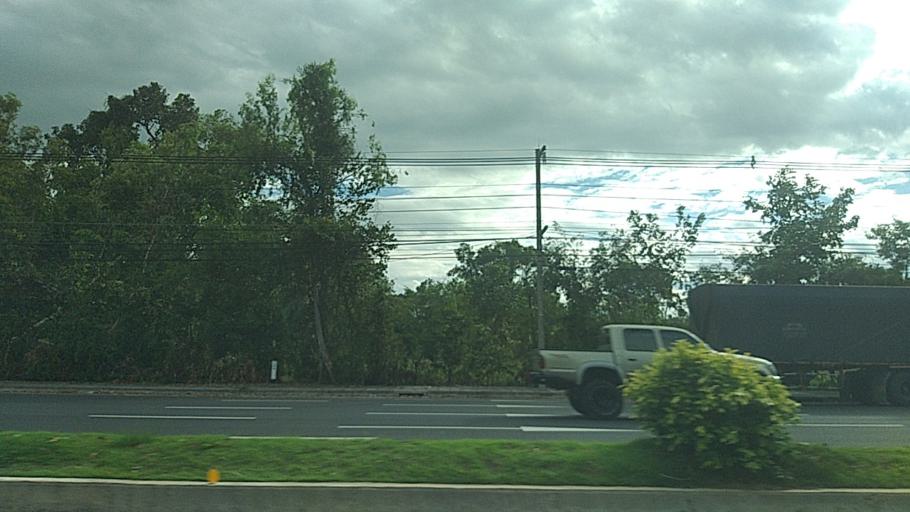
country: TH
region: Surin
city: Prasat
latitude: 14.6124
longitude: 103.4182
